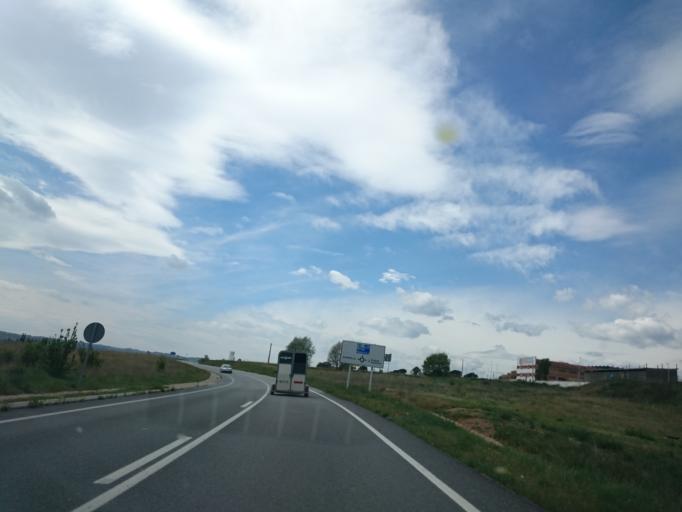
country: ES
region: Catalonia
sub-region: Provincia de Barcelona
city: Olvan
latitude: 42.0495
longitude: 1.8940
